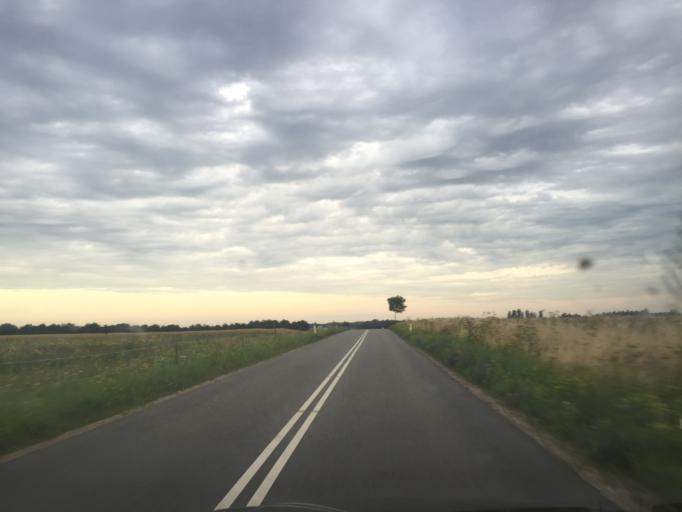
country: DK
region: Capital Region
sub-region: Egedal Kommune
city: Stenlose
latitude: 55.7326
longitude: 12.1945
